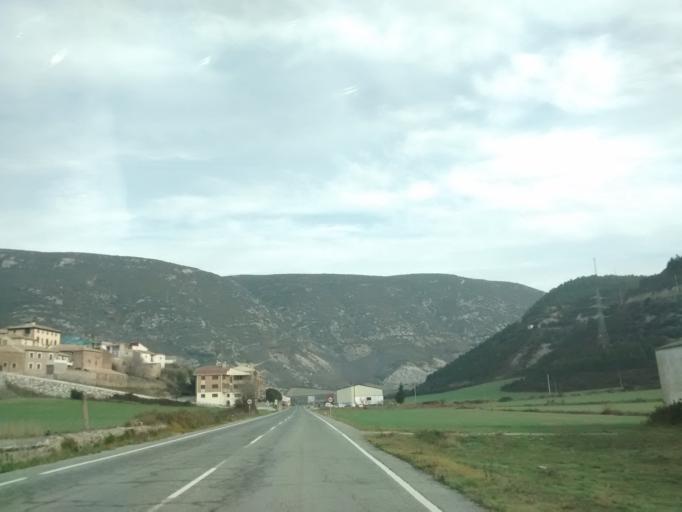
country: ES
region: Navarre
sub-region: Provincia de Navarra
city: Liedena
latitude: 42.6168
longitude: -1.2755
